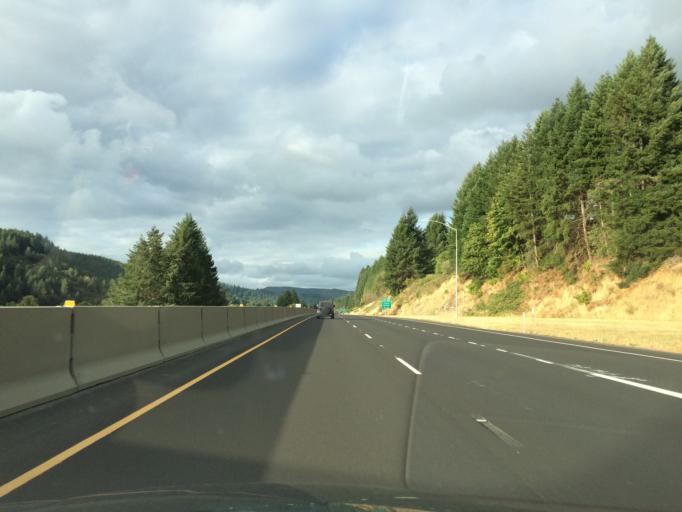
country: US
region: Oregon
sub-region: Douglas County
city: Drain
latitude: 43.7140
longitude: -123.2163
